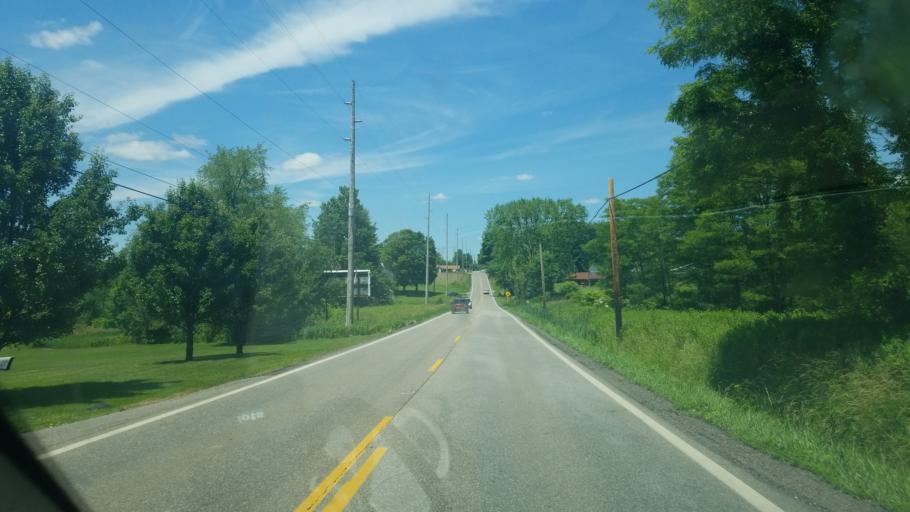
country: US
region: Ohio
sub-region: Columbiana County
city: Lisbon
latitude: 40.8160
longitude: -80.7960
